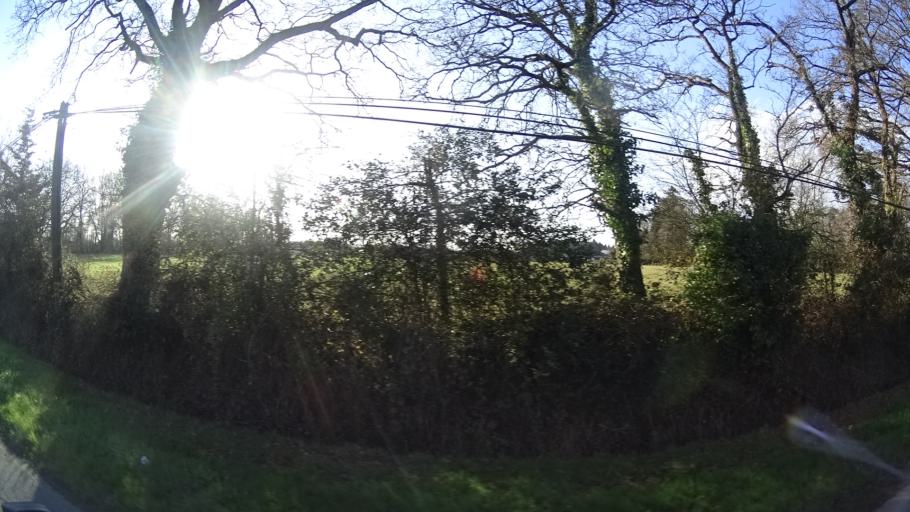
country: FR
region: Pays de la Loire
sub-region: Departement de la Loire-Atlantique
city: Plesse
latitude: 47.5333
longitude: -1.8870
